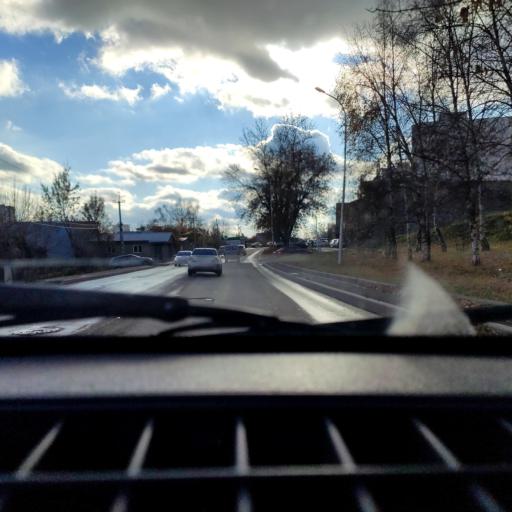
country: RU
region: Bashkortostan
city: Ufa
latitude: 54.7338
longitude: 55.9986
